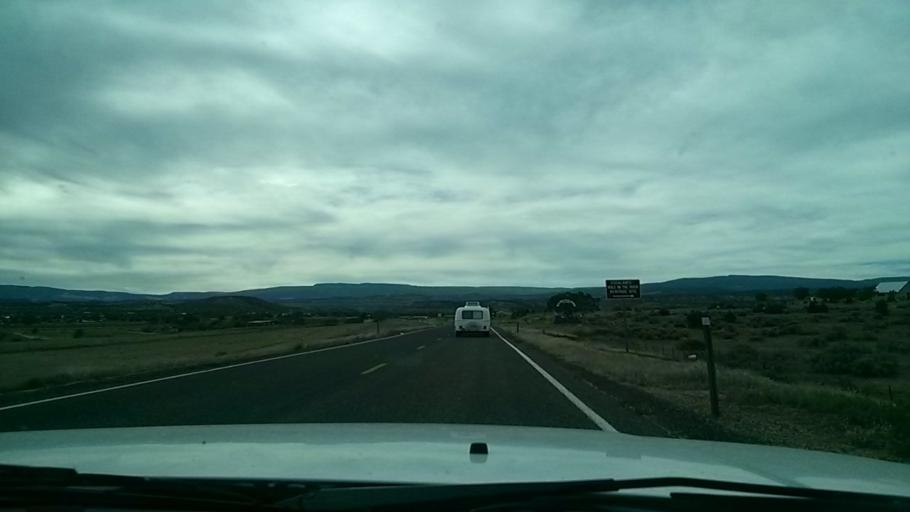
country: US
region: Utah
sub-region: Wayne County
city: Loa
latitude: 37.7600
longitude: -111.5764
